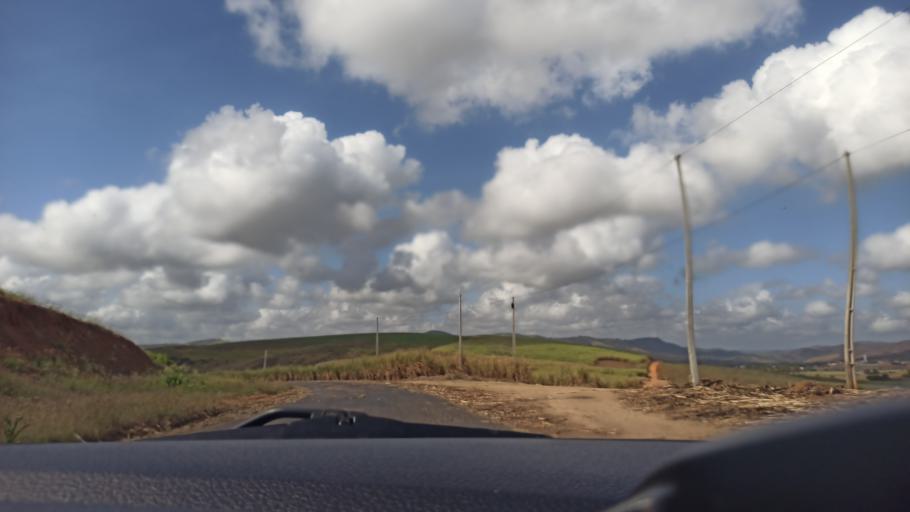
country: BR
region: Paraiba
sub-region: Juripiranga
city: Juripiranga
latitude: -7.3936
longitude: -35.2568
